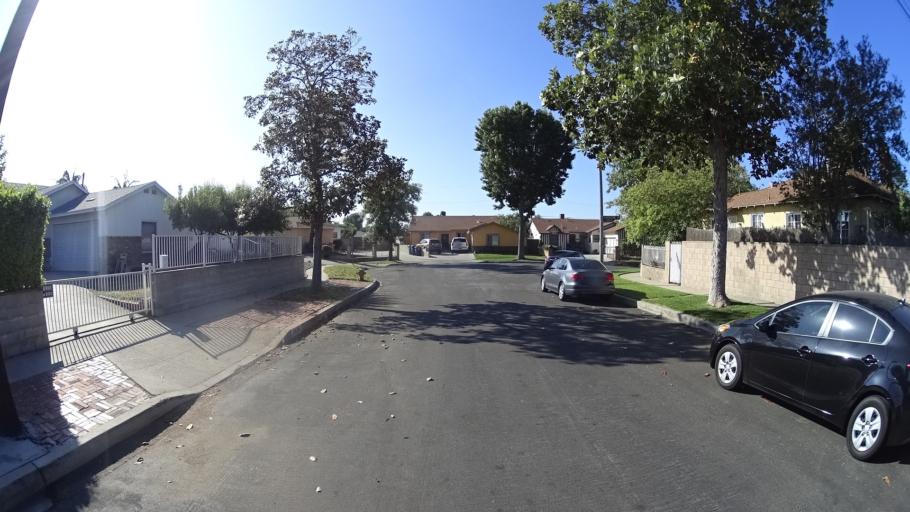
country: US
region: California
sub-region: Los Angeles County
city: Van Nuys
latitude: 34.2297
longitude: -118.4261
